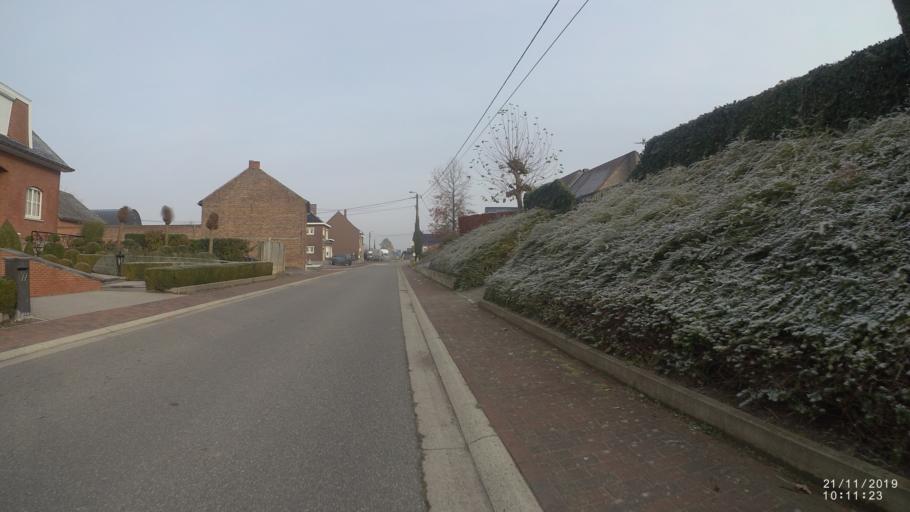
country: BE
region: Flanders
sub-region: Provincie Vlaams-Brabant
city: Zoutleeuw
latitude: 50.8162
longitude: 5.1119
